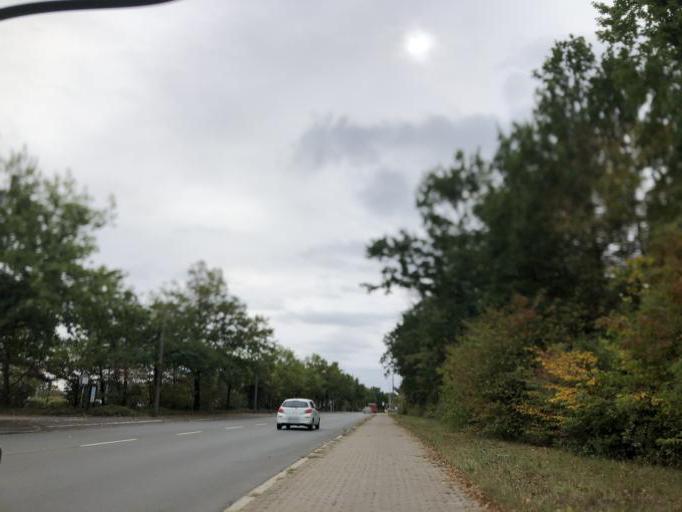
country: DE
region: Bavaria
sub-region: Regierungsbezirk Mittelfranken
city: Erlangen
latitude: 49.5810
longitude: 10.9668
